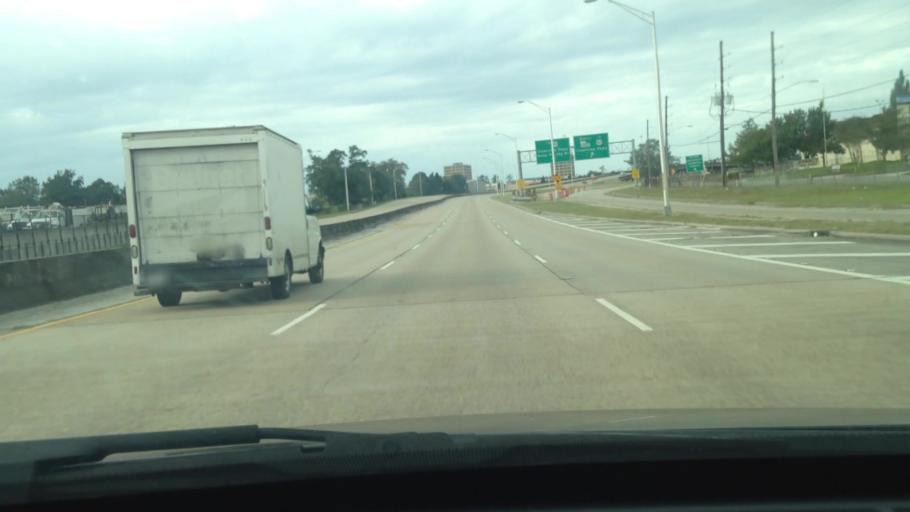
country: US
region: Louisiana
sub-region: Jefferson Parish
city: Metairie Terrace
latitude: 29.9704
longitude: -90.1770
